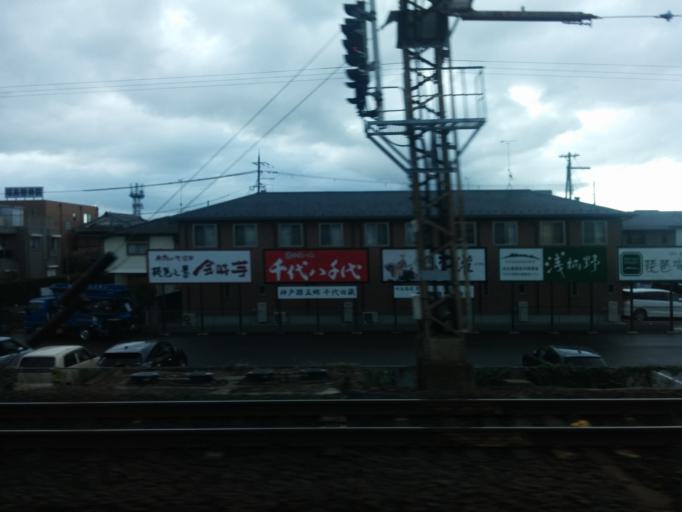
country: JP
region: Shiga Prefecture
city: Kusatsu
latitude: 35.0158
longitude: 135.9564
